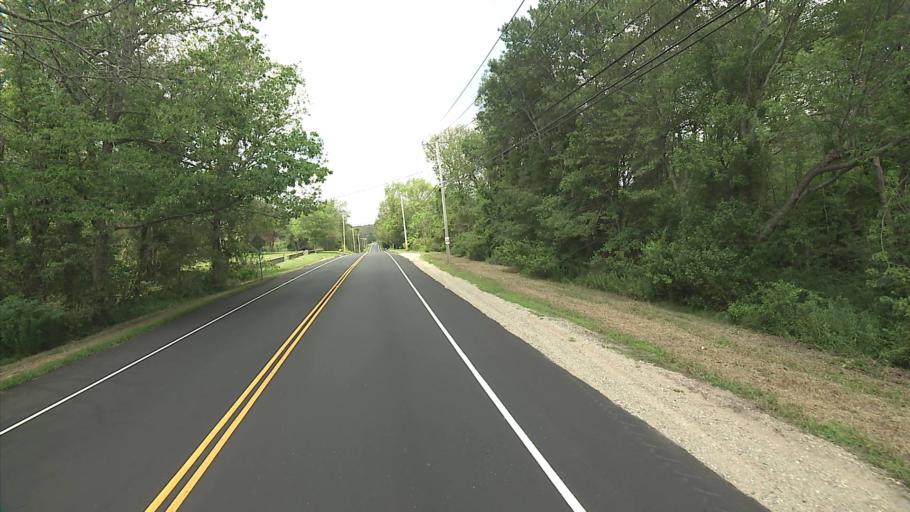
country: US
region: Connecticut
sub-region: New London County
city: Preston City
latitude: 41.5744
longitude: -71.8809
